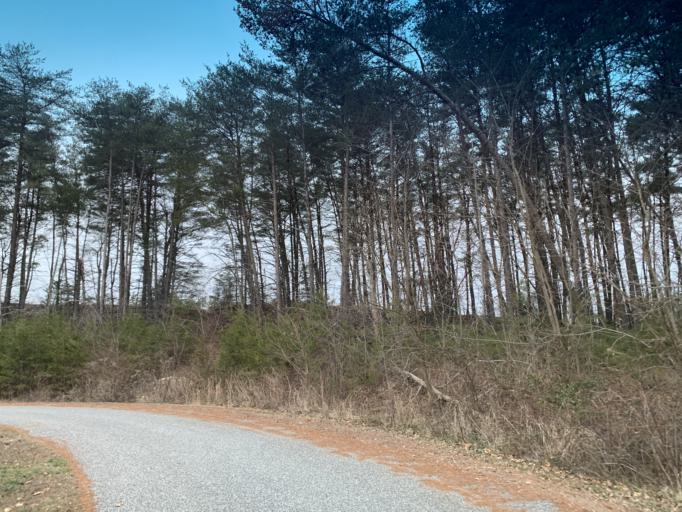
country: US
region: Maryland
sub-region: Baltimore County
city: Carney
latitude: 39.3905
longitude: -76.4988
